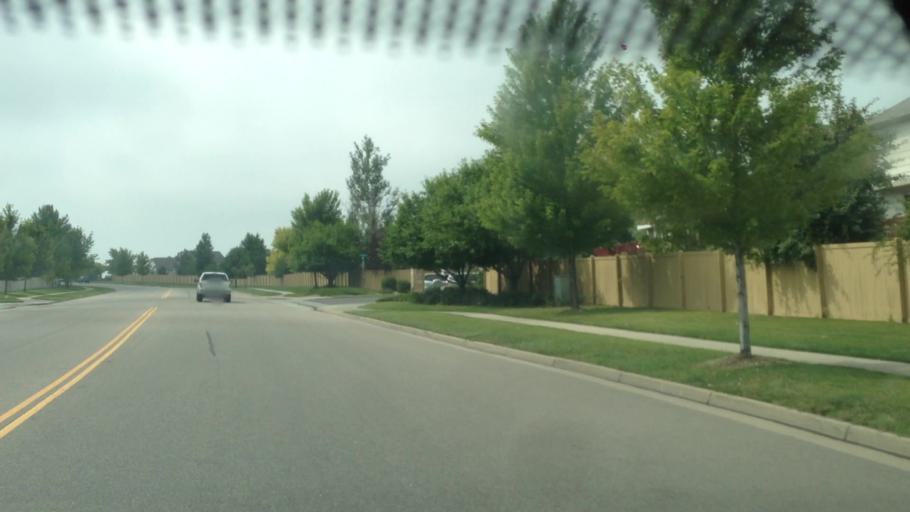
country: US
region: Colorado
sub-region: Douglas County
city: Parker
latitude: 39.6088
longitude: -104.7305
